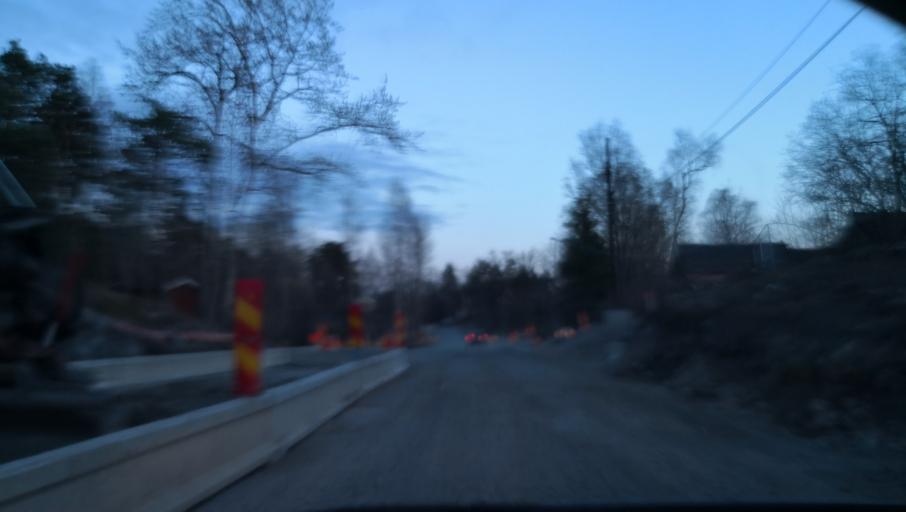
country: SE
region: Stockholm
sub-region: Nacka Kommun
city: Kummelnas
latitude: 59.3451
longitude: 18.2910
